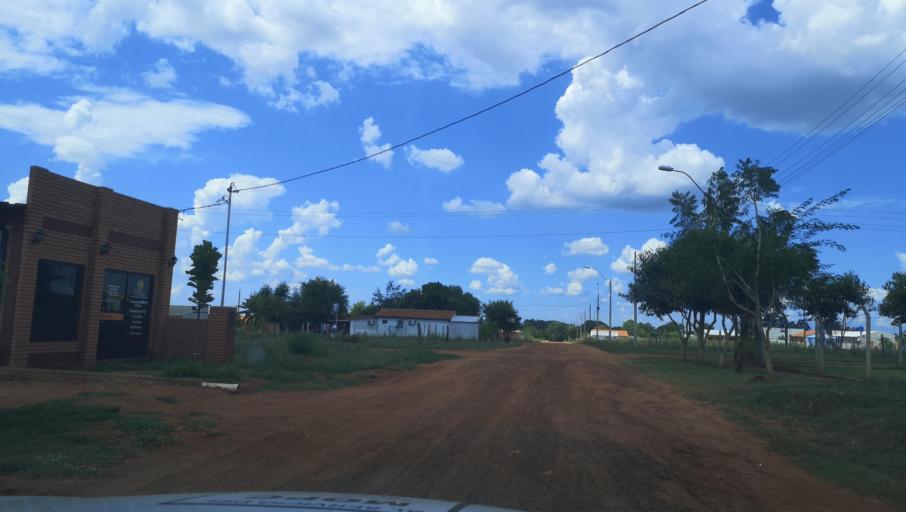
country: PY
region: Misiones
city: Santa Maria
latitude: -26.8925
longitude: -57.0384
